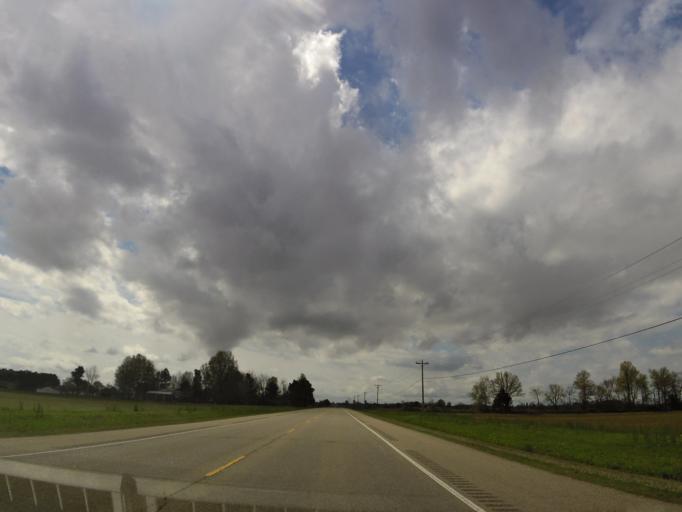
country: US
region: Arkansas
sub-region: Clay County
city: Corning
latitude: 36.4457
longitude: -90.5856
